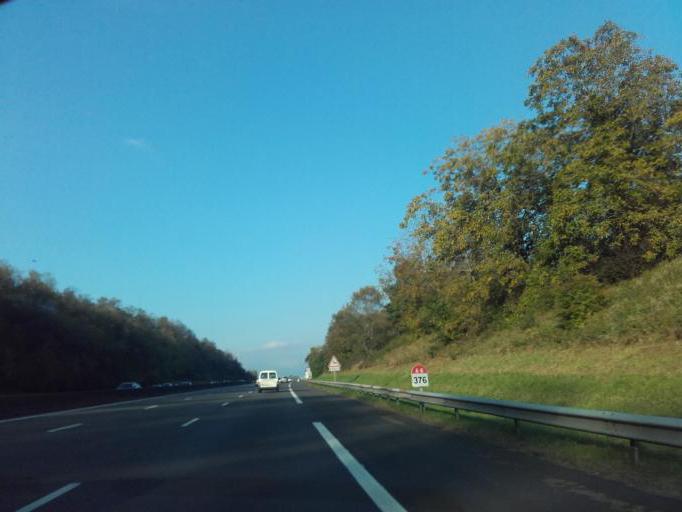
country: FR
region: Bourgogne
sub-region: Departement de Saone-et-Loire
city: Saint-Martin-Belle-Roche
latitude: 46.4092
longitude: 4.8584
